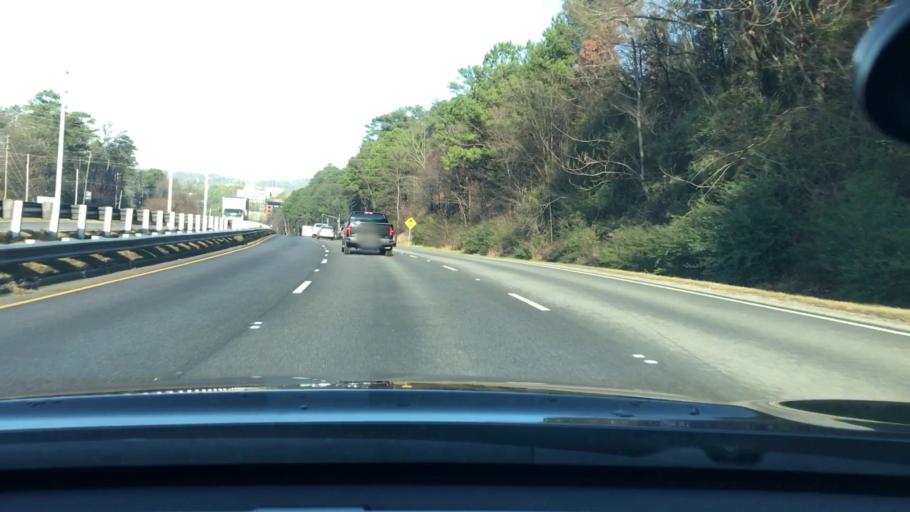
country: US
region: Alabama
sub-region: Jefferson County
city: Cahaba Heights
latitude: 33.4691
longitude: -86.7584
